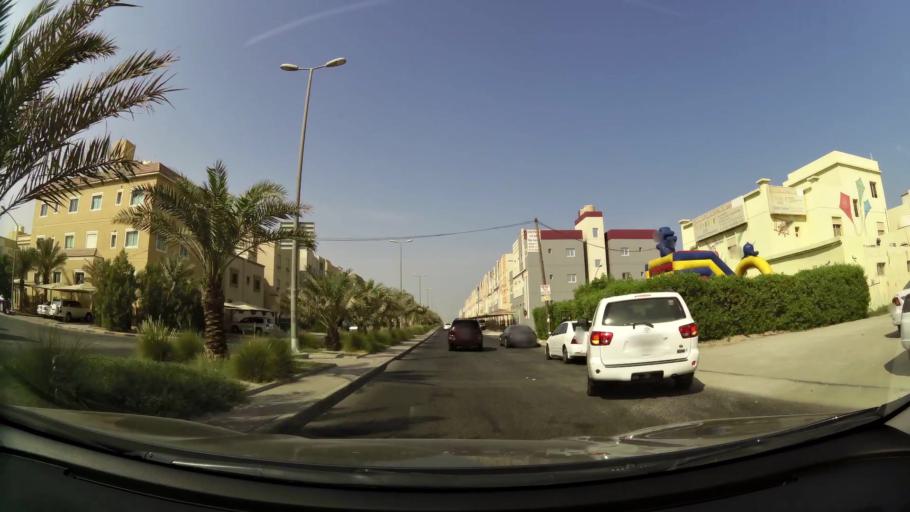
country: KW
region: Al Ahmadi
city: Al Manqaf
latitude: 29.1130
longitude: 48.1229
